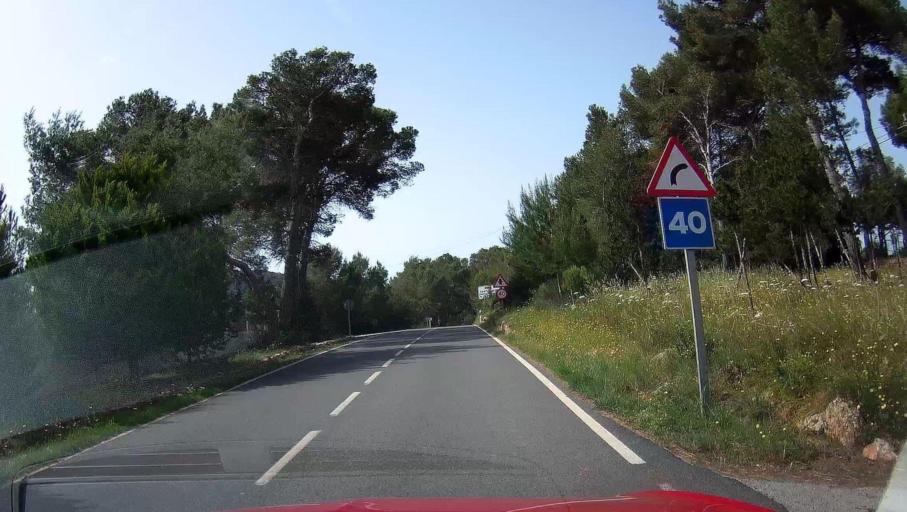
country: ES
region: Balearic Islands
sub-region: Illes Balears
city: Sant Joan de Labritja
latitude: 39.0478
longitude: 1.5708
